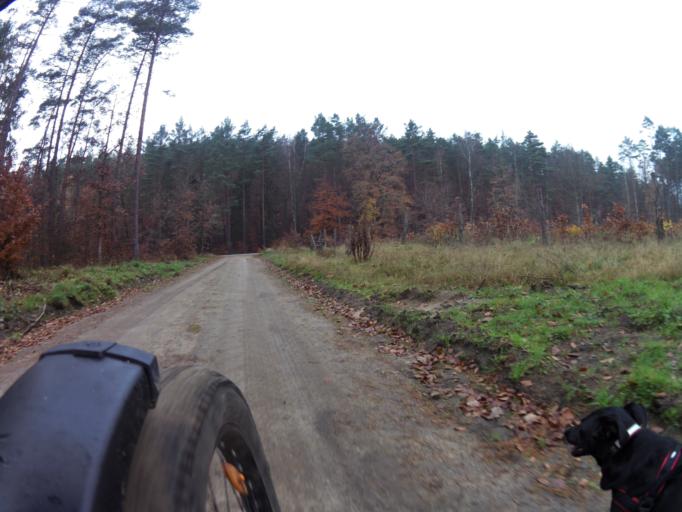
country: PL
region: Pomeranian Voivodeship
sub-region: Powiat wejherowski
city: Orle
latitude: 54.7034
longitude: 18.1538
